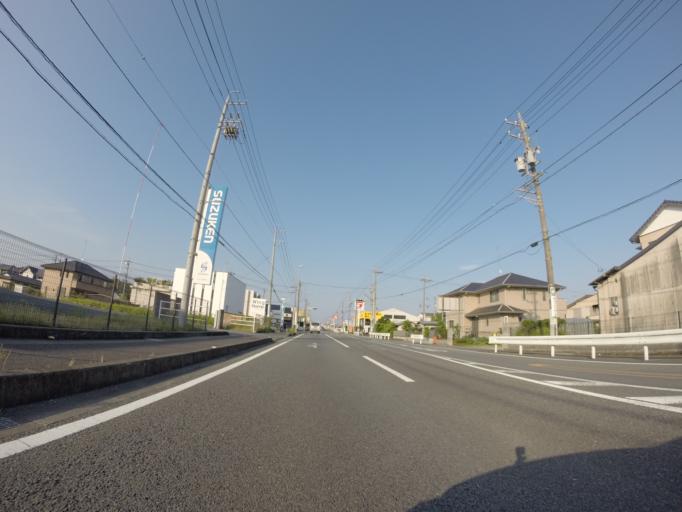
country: JP
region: Shizuoka
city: Kakegawa
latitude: 34.7781
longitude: 138.0295
